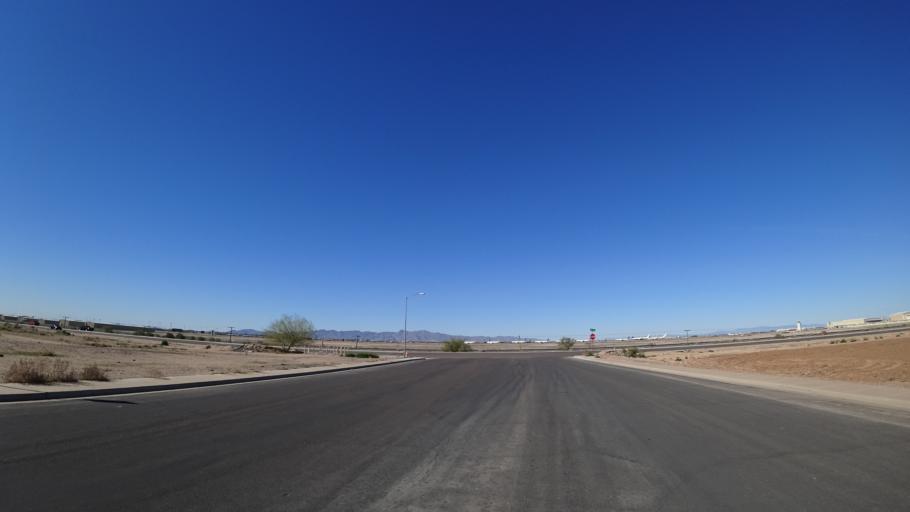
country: US
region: Arizona
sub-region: Maricopa County
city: Goodyear
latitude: 33.4167
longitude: -112.3704
